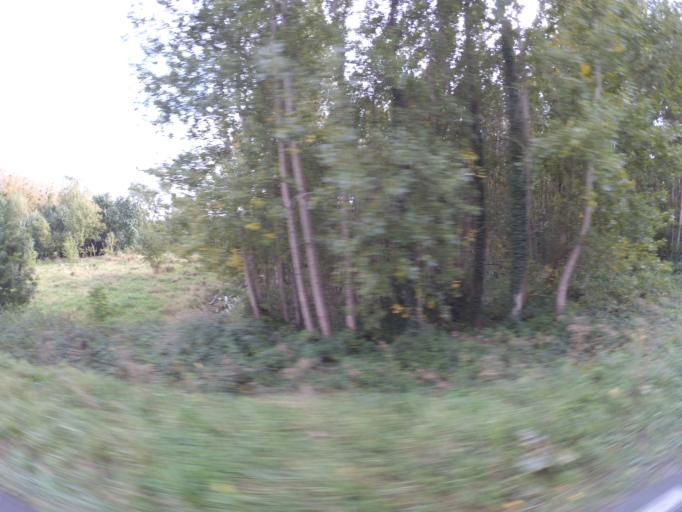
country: FR
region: Centre
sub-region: Departement d'Indre-et-Loire
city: Langeais
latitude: 47.3121
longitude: 0.3697
